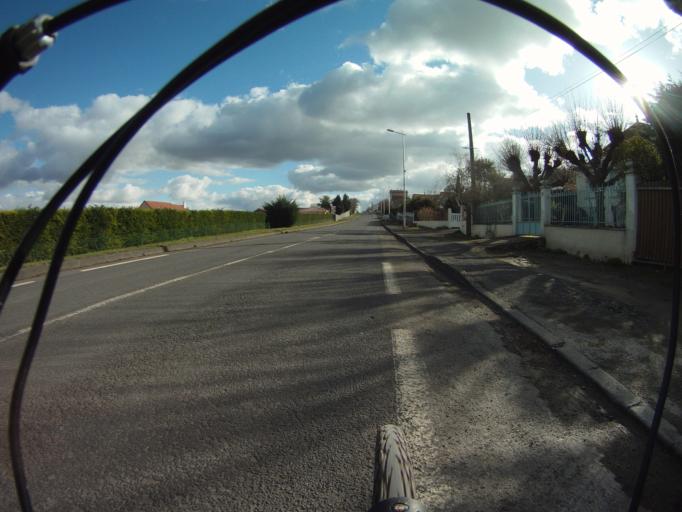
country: FR
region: Auvergne
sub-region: Departement du Puy-de-Dome
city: Perignat-les-Sarlieve
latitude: 45.7336
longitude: 3.1424
